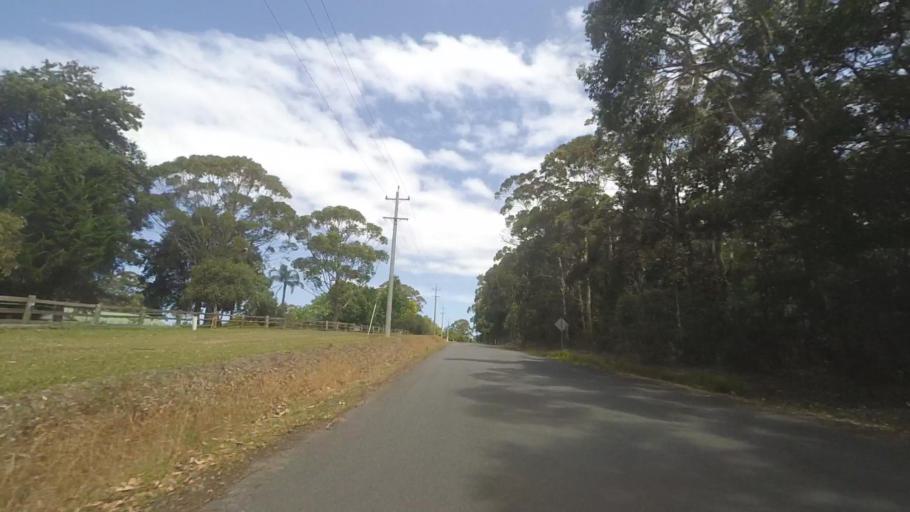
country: AU
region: New South Wales
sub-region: Shoalhaven Shire
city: Milton
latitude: -35.3947
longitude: 150.3690
